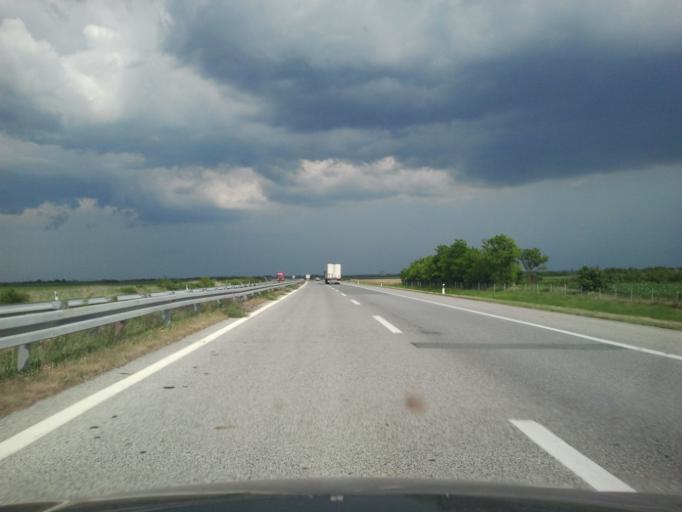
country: RS
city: Radenkovic
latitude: 45.0220
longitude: 19.4959
